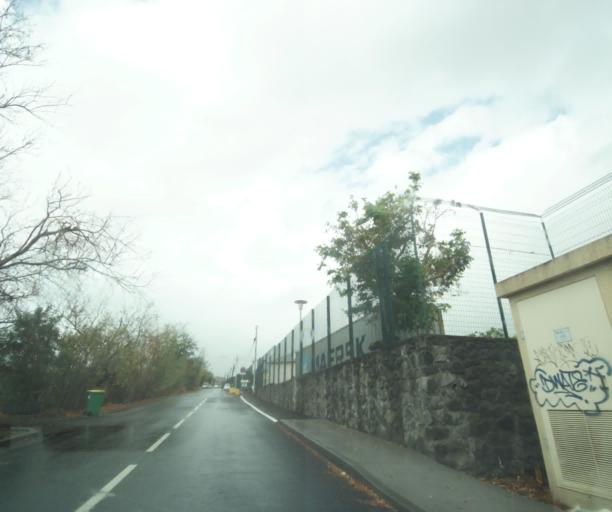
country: RE
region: Reunion
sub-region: Reunion
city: Le Port
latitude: -20.9757
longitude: 55.2995
